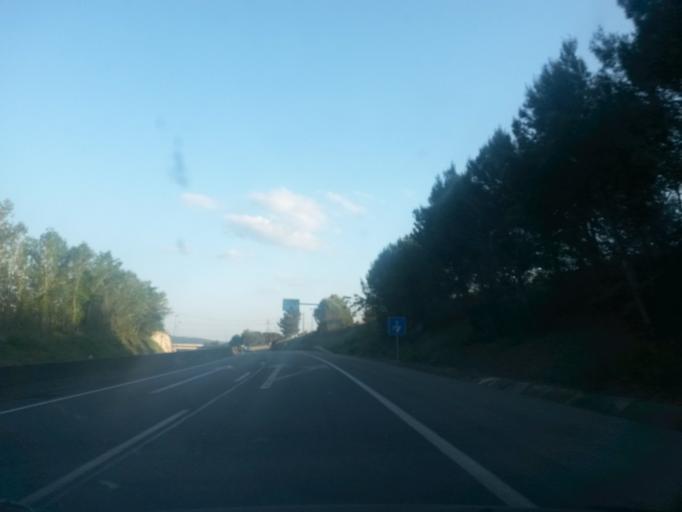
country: ES
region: Catalonia
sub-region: Provincia de Girona
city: Palol de Revardit
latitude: 42.0606
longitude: 2.8127
